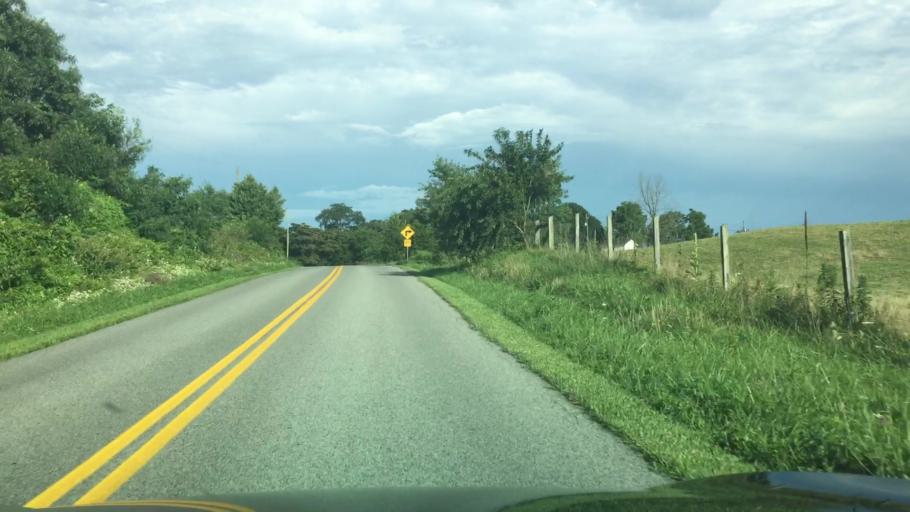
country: US
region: Virginia
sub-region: Wythe County
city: Wytheville
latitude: 36.9369
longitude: -80.9506
